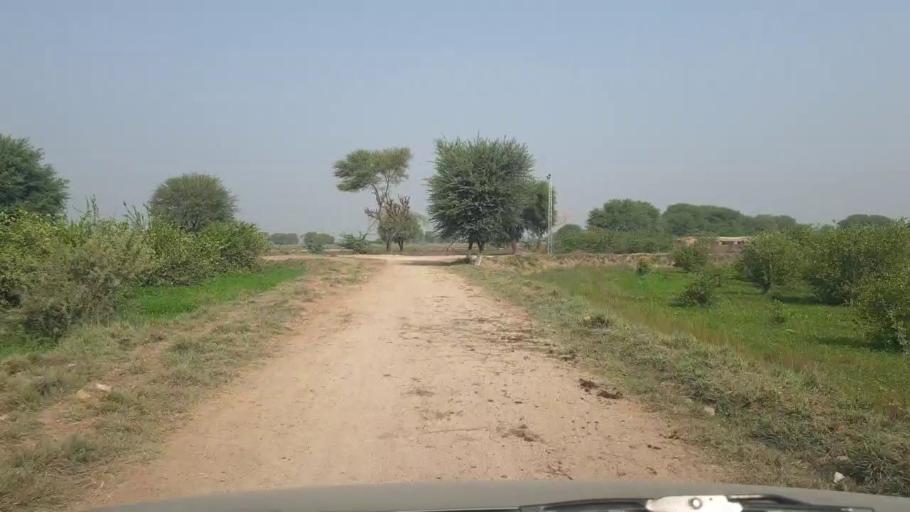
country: PK
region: Sindh
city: Umarkot
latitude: 25.3940
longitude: 69.7094
